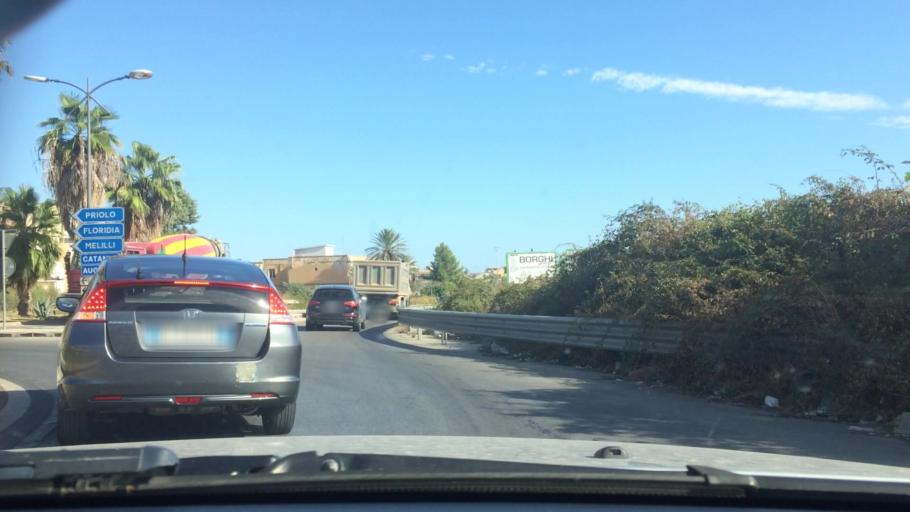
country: IT
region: Sicily
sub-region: Provincia di Siracusa
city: Priolo Gargallo
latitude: 37.1535
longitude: 15.1910
